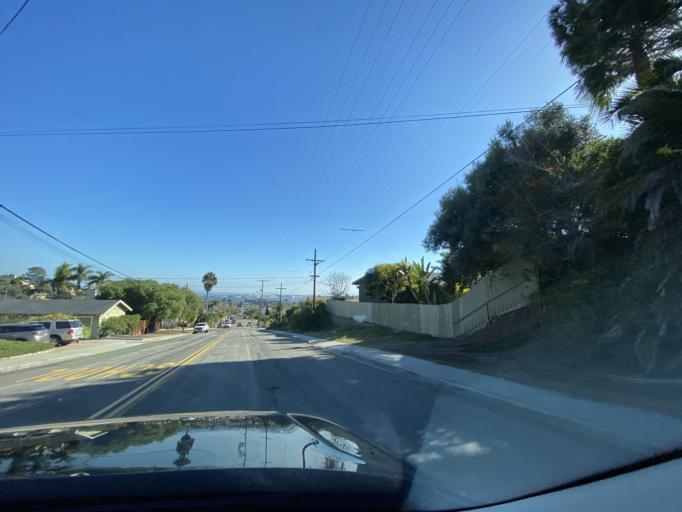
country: US
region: California
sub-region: San Diego County
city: Coronado
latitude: 32.7326
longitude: -117.2309
